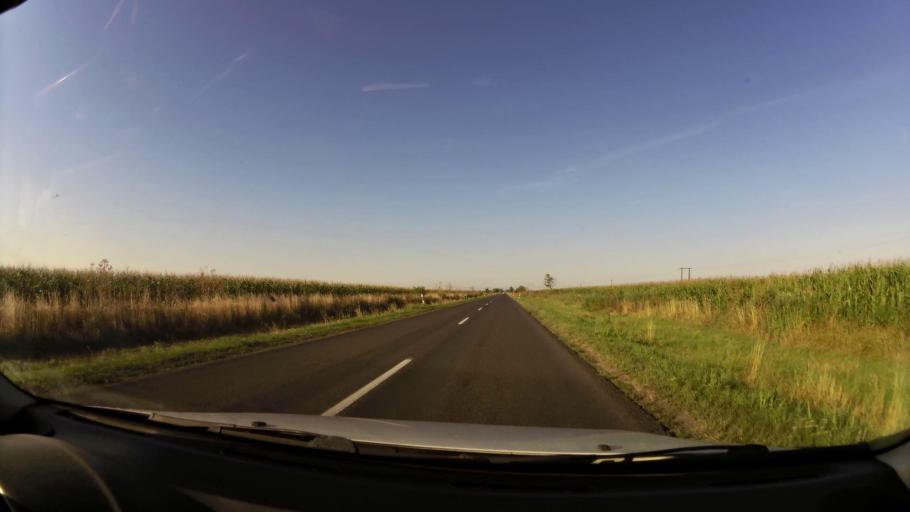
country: HU
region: Pest
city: Tapioszolos
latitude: 47.2488
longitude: 19.8475
